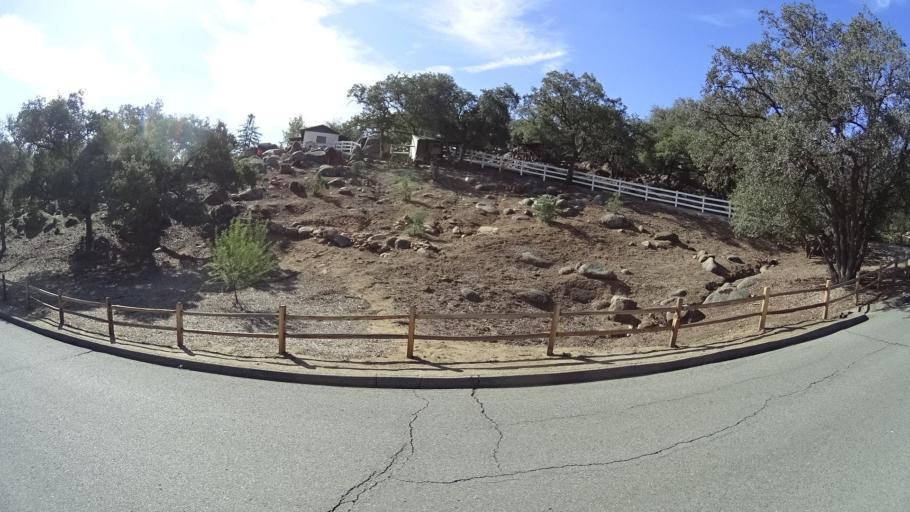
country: US
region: California
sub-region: San Diego County
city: Alpine
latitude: 32.8204
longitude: -116.7554
